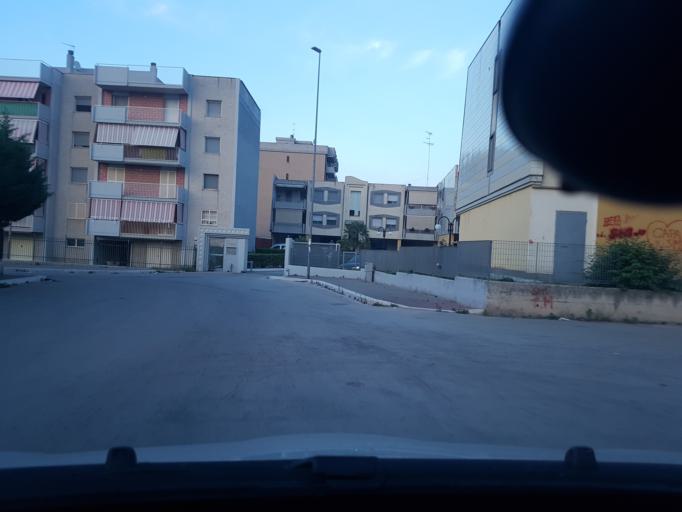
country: IT
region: Apulia
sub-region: Provincia di Foggia
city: Cerignola
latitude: 41.2619
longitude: 15.8800
